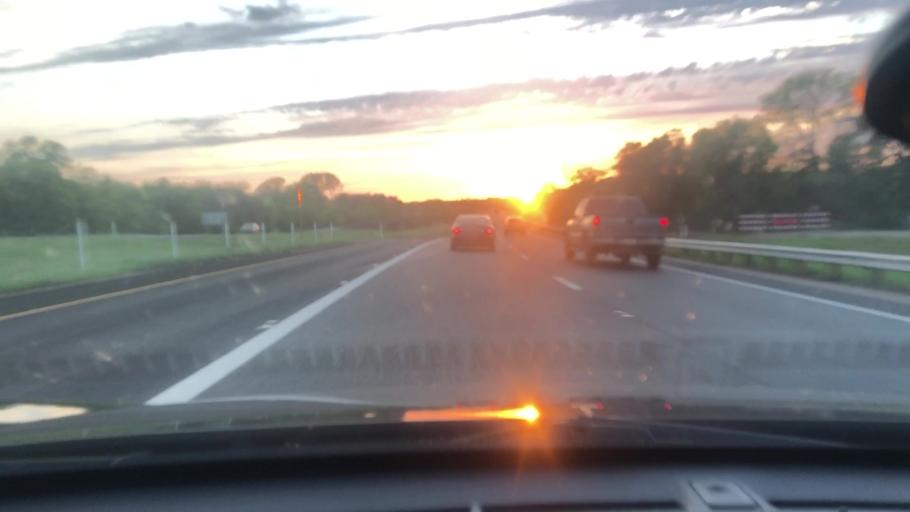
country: US
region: Texas
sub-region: Jackson County
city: Edna
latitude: 28.9603
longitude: -96.6834
